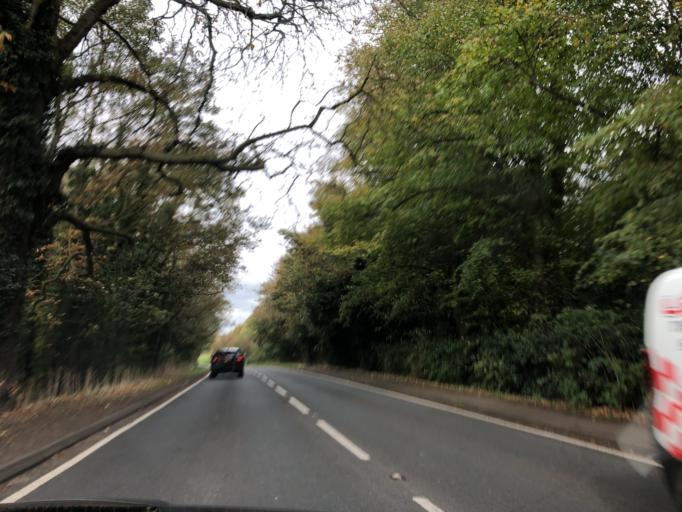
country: GB
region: England
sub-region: Warwickshire
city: Royal Leamington Spa
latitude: 52.3147
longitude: -1.5403
